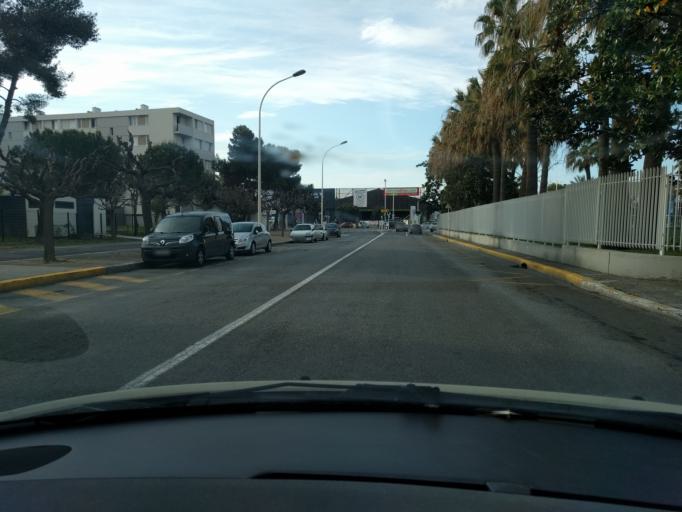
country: FR
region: Provence-Alpes-Cote d'Azur
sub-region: Departement des Alpes-Maritimes
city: Mandelieu-la-Napoule
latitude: 43.5509
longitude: 6.9661
